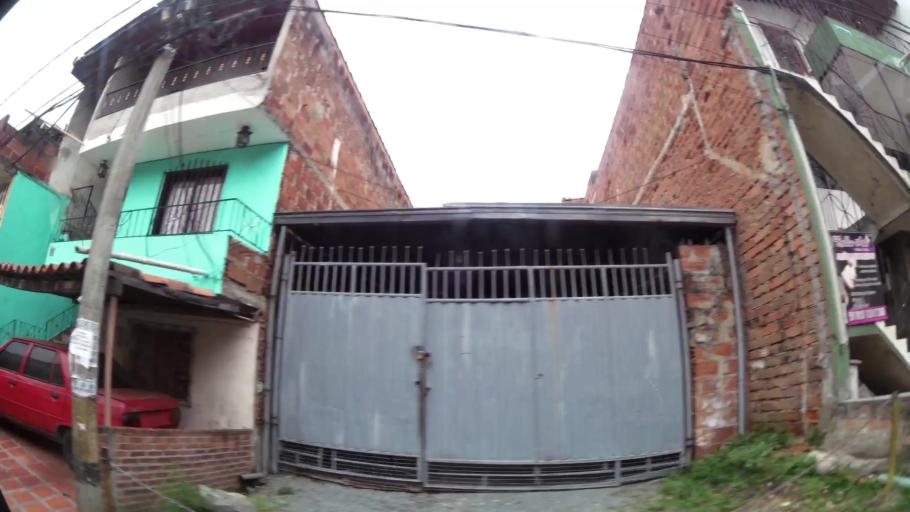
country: CO
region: Antioquia
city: Medellin
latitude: 6.2847
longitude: -75.5871
